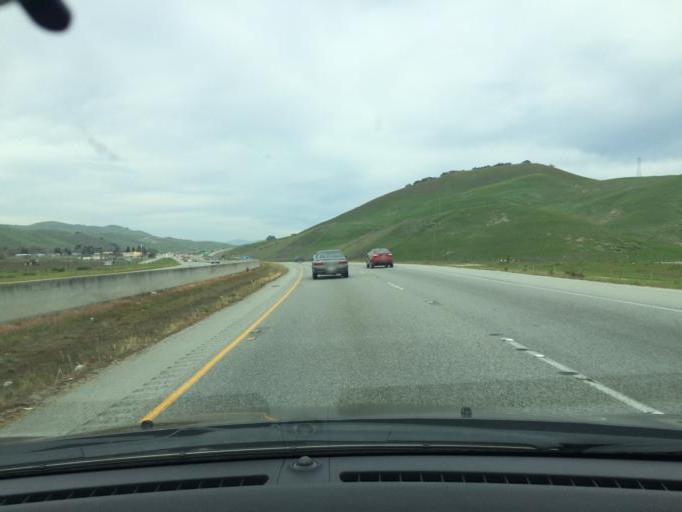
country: US
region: California
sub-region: San Benito County
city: San Juan Bautista
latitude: 36.8912
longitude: -121.5565
